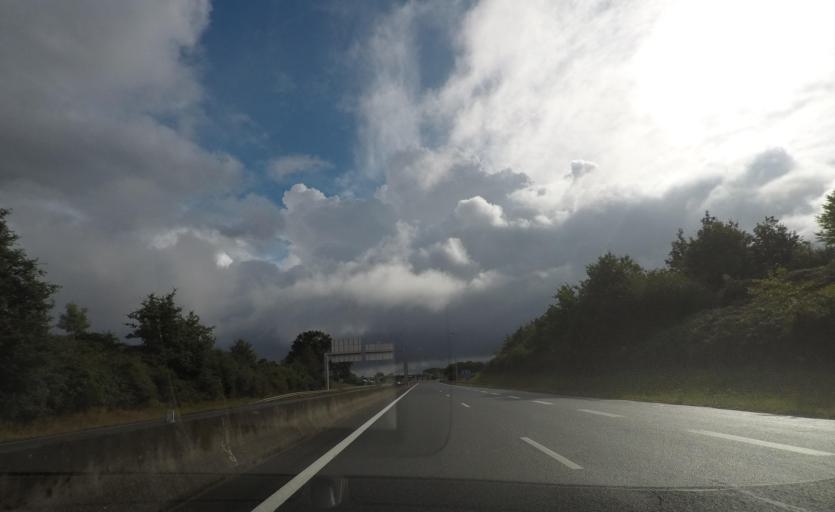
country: FR
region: Pays de la Loire
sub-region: Departement de la Vendee
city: La Ferriere
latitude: 46.6710
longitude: -1.3510
